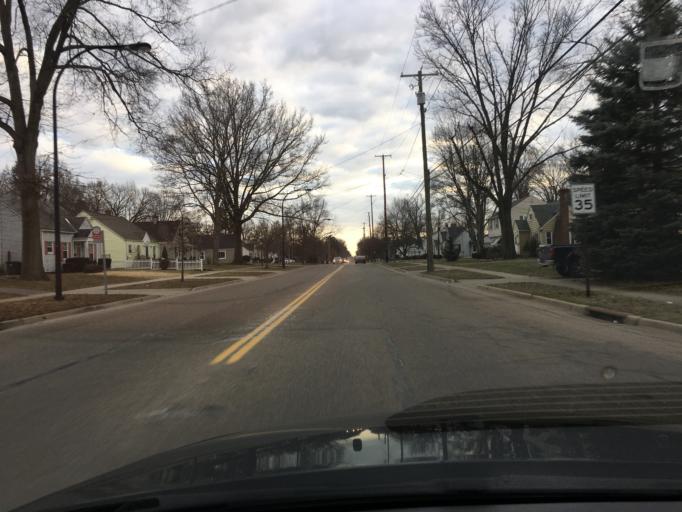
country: US
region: Ohio
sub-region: Summit County
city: Fairlawn
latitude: 41.1033
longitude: -81.5693
